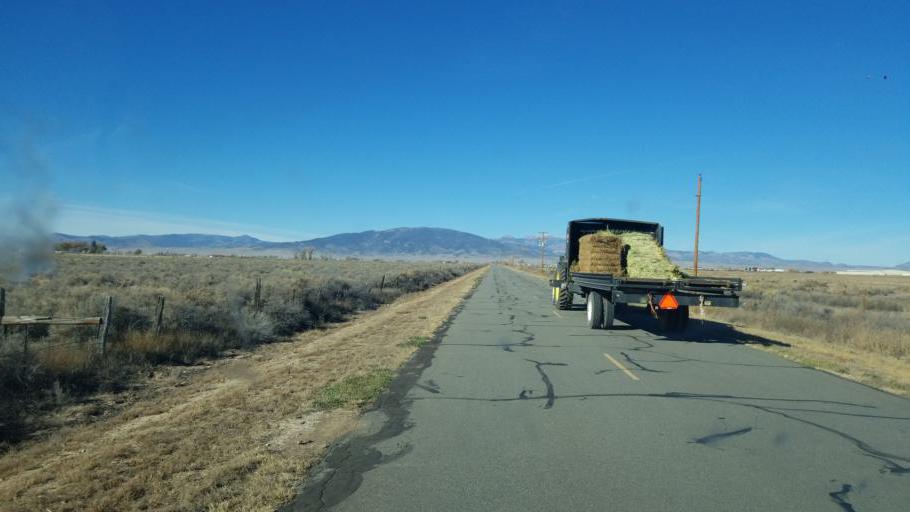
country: US
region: Colorado
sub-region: Alamosa County
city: Alamosa
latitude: 37.4586
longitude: -106.0269
